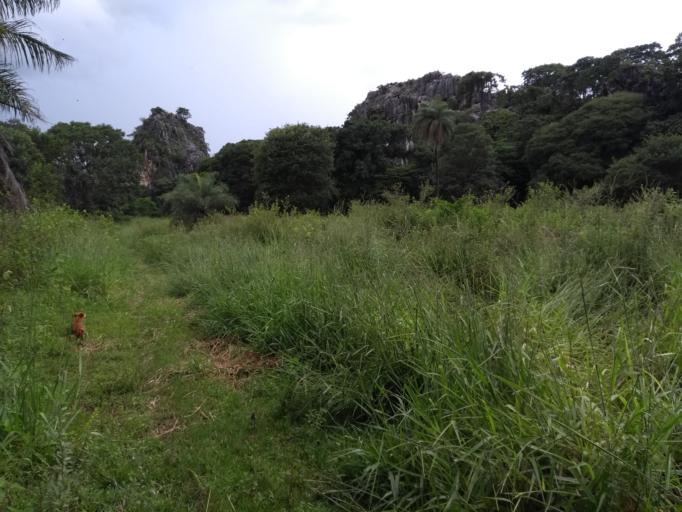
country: BR
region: Goias
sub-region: Formosa
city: Formosa
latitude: -15.4944
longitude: -47.3018
